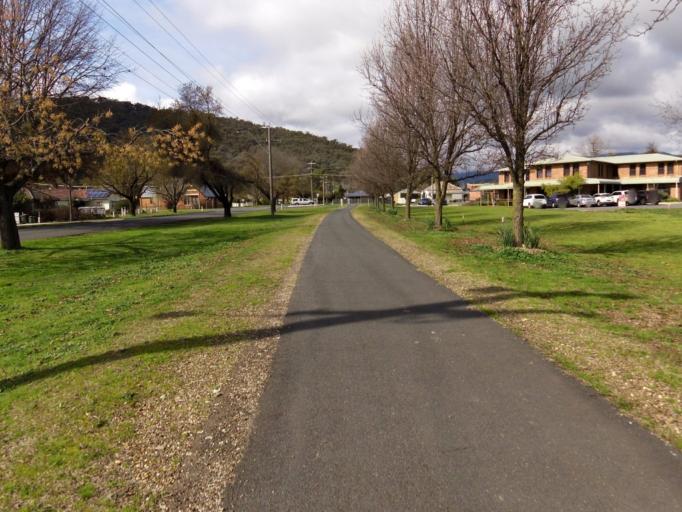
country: AU
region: Victoria
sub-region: Wangaratta
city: Wangaratta
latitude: -36.5616
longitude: 146.7278
